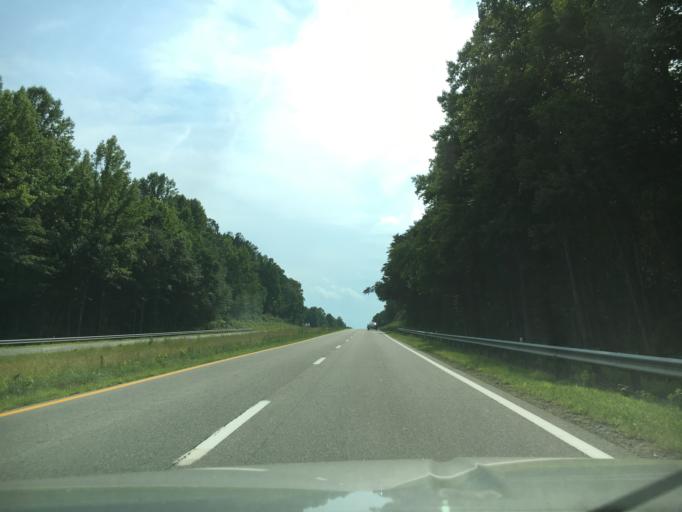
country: US
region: Virginia
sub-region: Halifax County
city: Halifax
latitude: 36.8222
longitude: -78.7146
